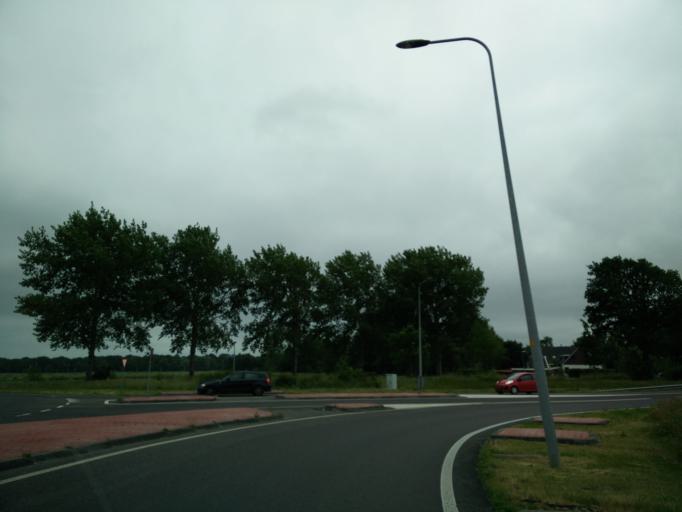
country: NL
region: Groningen
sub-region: Gemeente Groningen
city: Groningen
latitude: 53.1972
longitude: 6.5123
